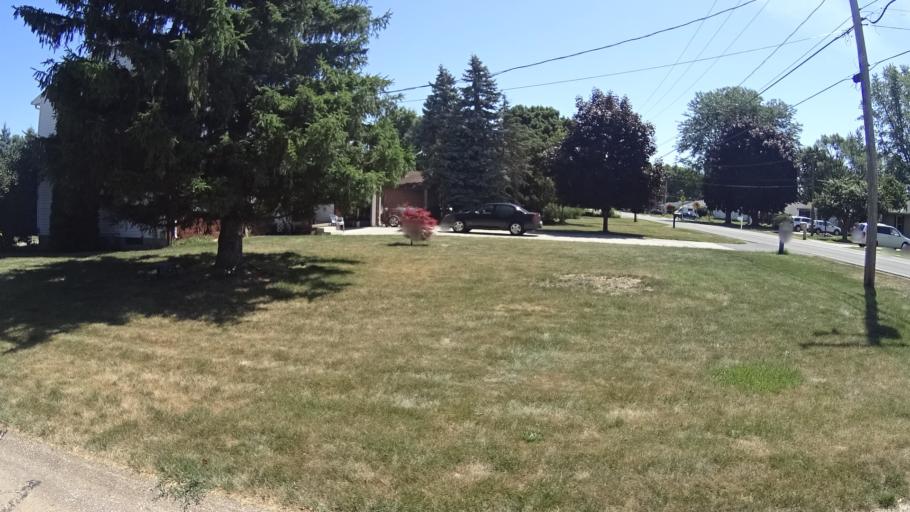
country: US
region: Ohio
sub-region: Erie County
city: Sandusky
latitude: 41.4170
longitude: -82.7003
